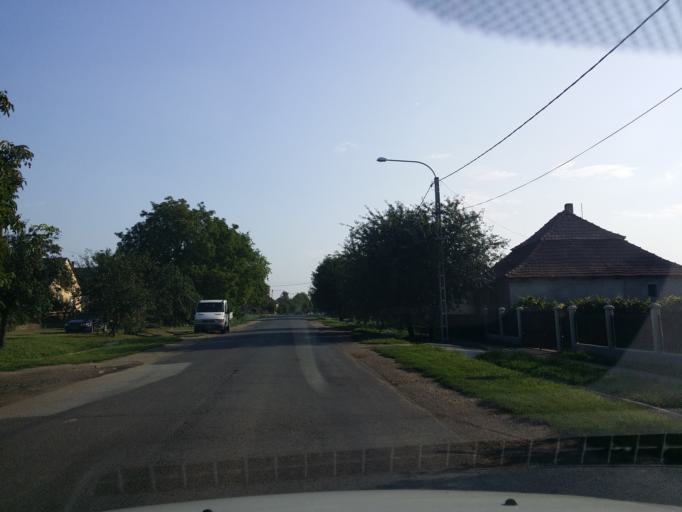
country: HU
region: Borsod-Abauj-Zemplen
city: Gonc
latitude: 48.3900
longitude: 21.2201
